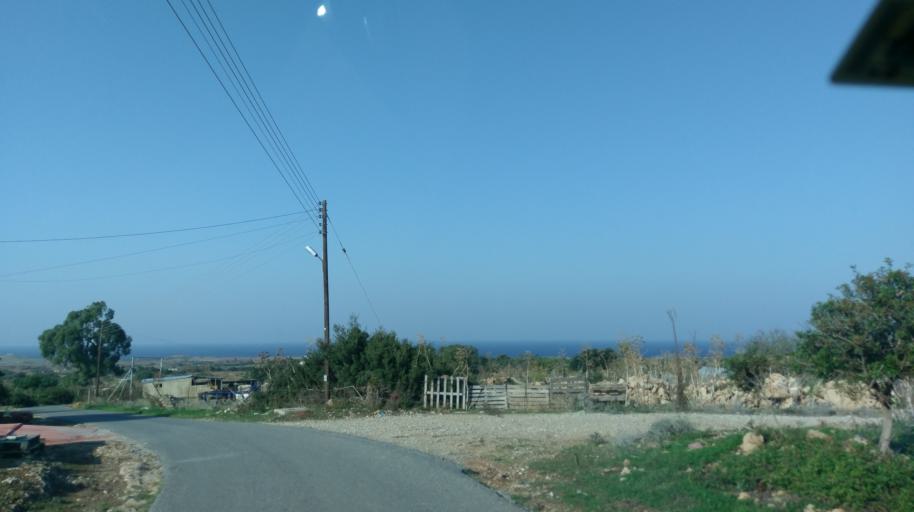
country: CY
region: Ammochostos
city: Leonarisso
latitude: 35.5424
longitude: 34.1879
